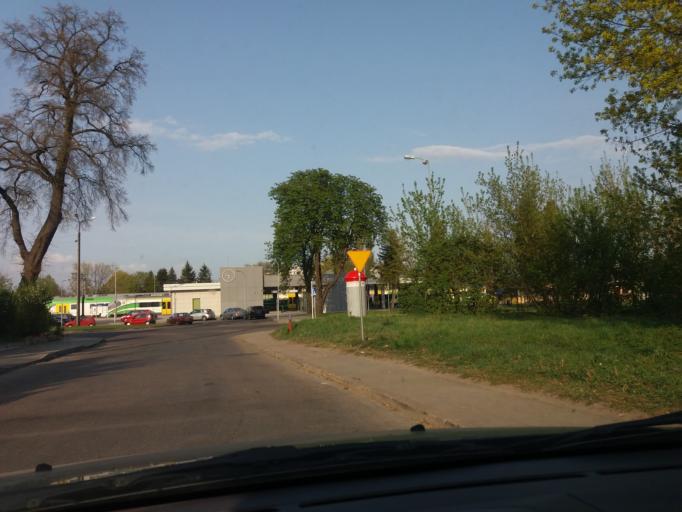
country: PL
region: Masovian Voivodeship
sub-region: Powiat mlawski
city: Mlawa
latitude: 53.1268
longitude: 20.3487
